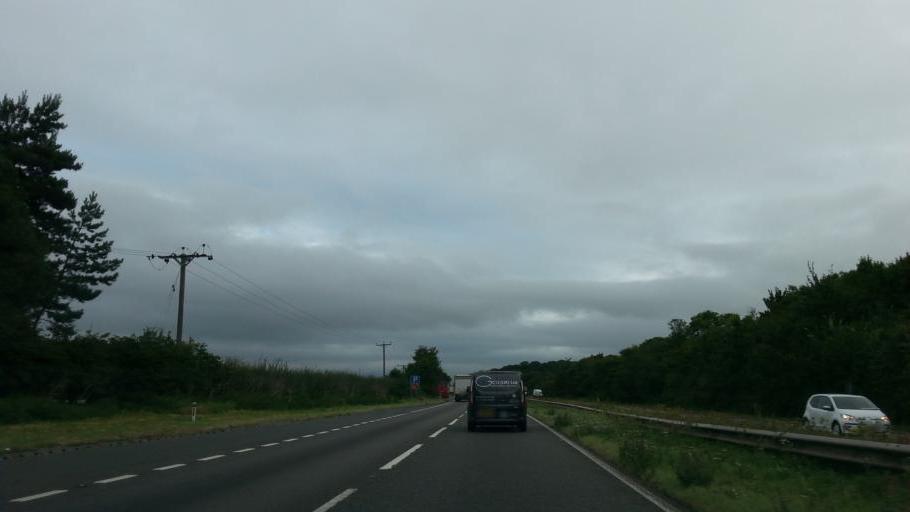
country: GB
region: England
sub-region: Nottinghamshire
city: Babworth
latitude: 53.3266
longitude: -1.0275
